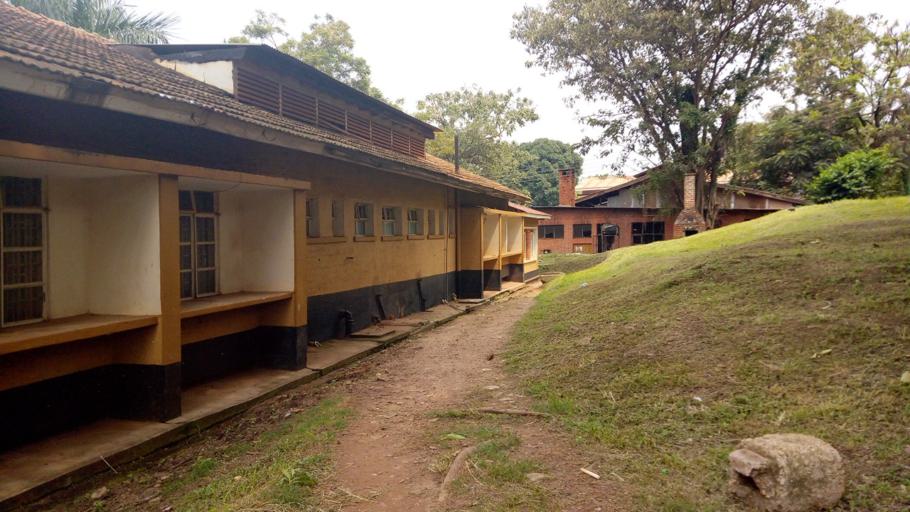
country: UG
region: Central Region
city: Kampala Central Division
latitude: 0.3289
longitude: 32.5698
